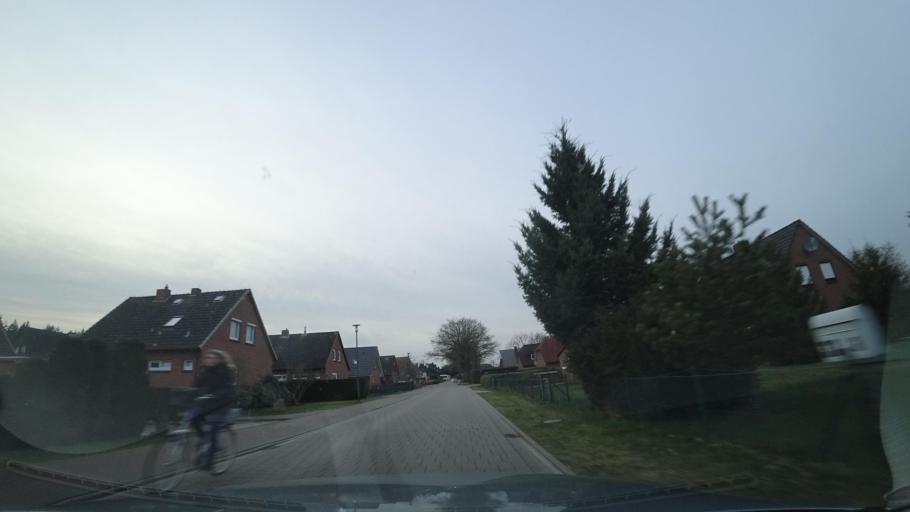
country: DE
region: Lower Saxony
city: Wardenburg
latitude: 53.0448
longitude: 8.2766
